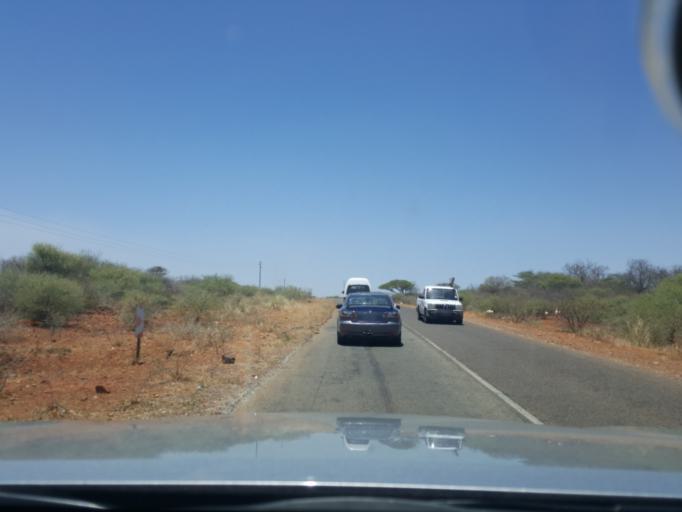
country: ZA
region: North-West
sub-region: Ngaka Modiri Molema District Municipality
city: Zeerust
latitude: -25.3887
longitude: 25.9352
